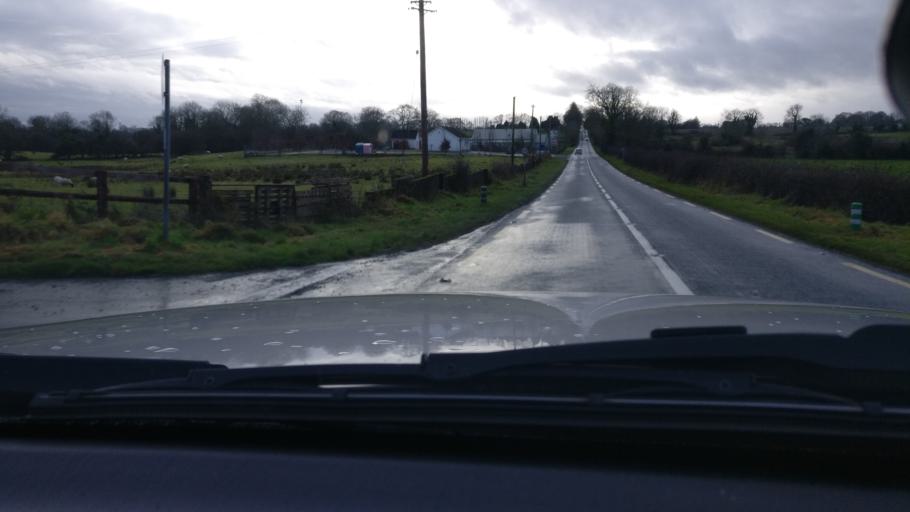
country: IE
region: Leinster
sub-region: An Iarmhi
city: Moate
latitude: 53.6099
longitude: -7.7087
